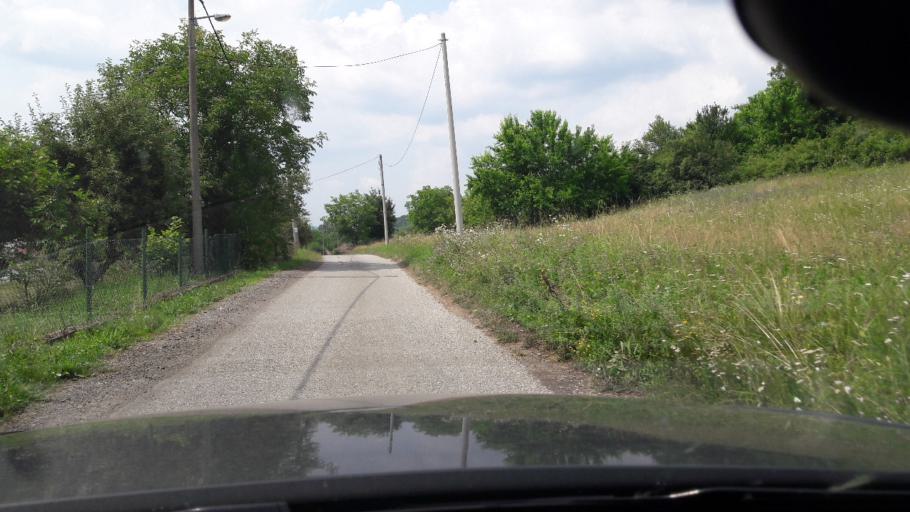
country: RS
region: Central Serbia
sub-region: Belgrade
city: Sopot
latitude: 44.6295
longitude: 20.5954
